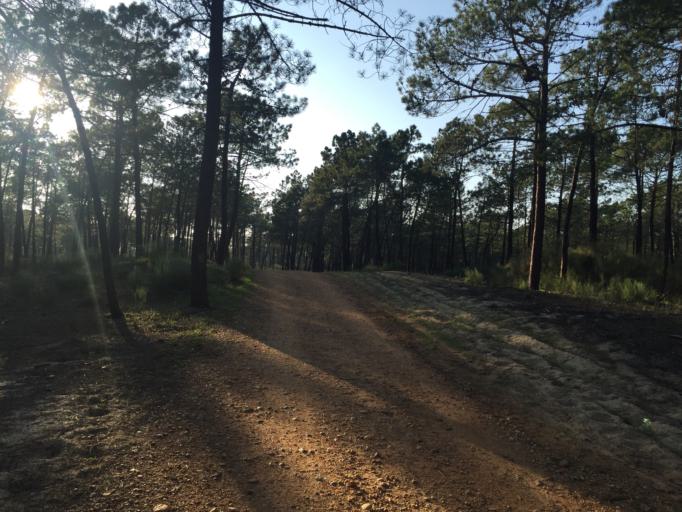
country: PT
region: Faro
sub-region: Vila Real de Santo Antonio
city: Monte Gordo
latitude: 37.1847
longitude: -7.4392
